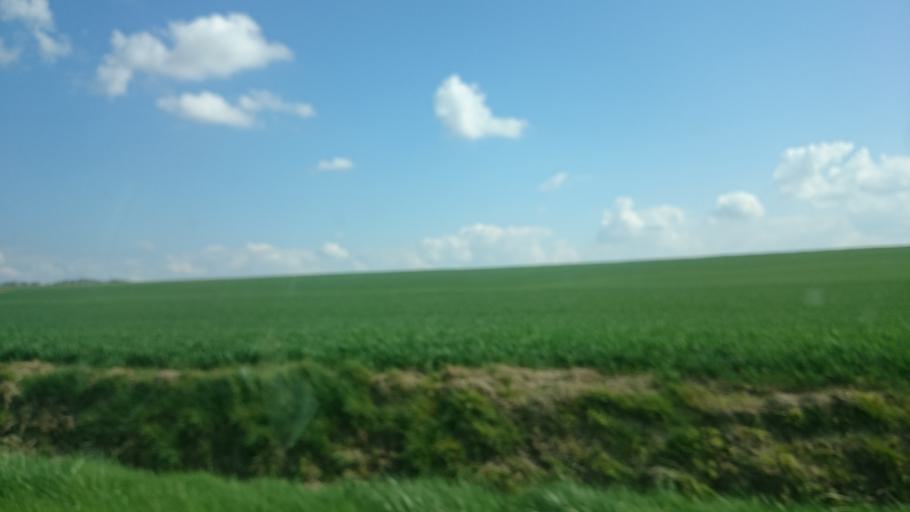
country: FR
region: Picardie
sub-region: Departement de l'Aisne
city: Origny-Sainte-Benoite
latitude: 49.8577
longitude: 3.5365
